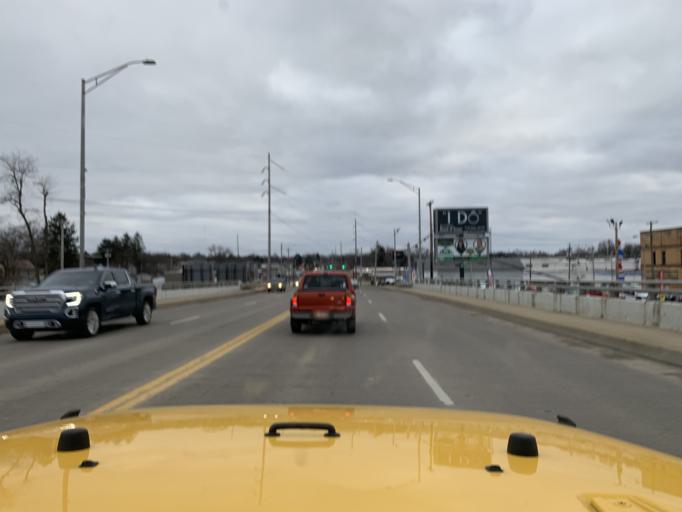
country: US
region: Ohio
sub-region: Tuscarawas County
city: Dover
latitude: 40.5201
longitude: -81.4736
